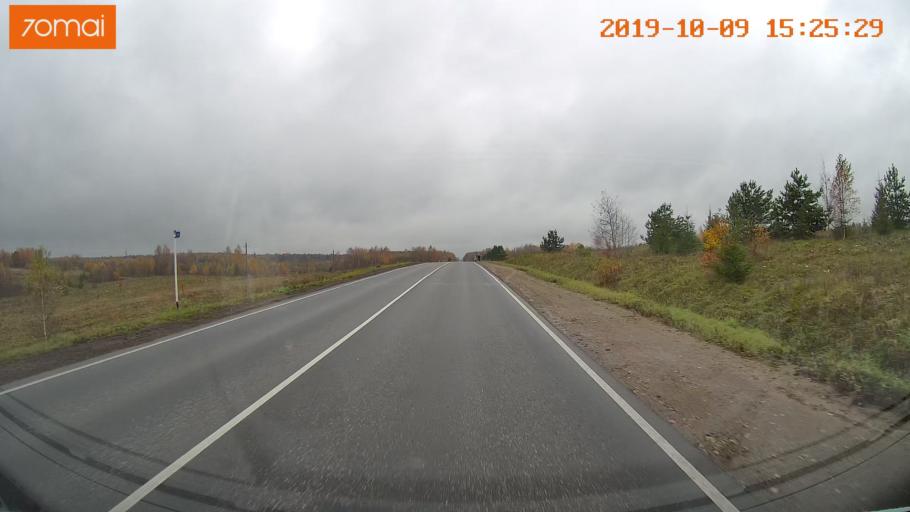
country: RU
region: Kostroma
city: Susanino
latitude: 58.0266
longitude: 41.4272
